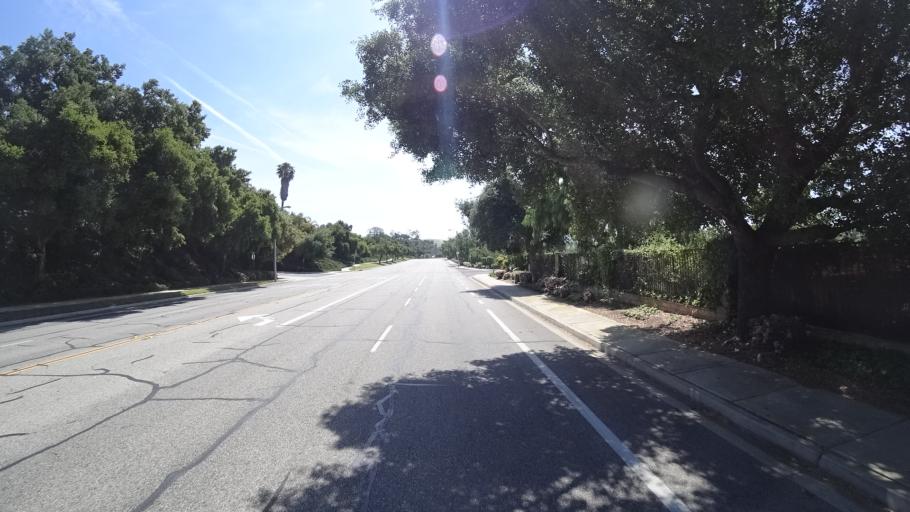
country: US
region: California
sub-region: Ventura County
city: Thousand Oaks
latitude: 34.1985
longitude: -118.8501
